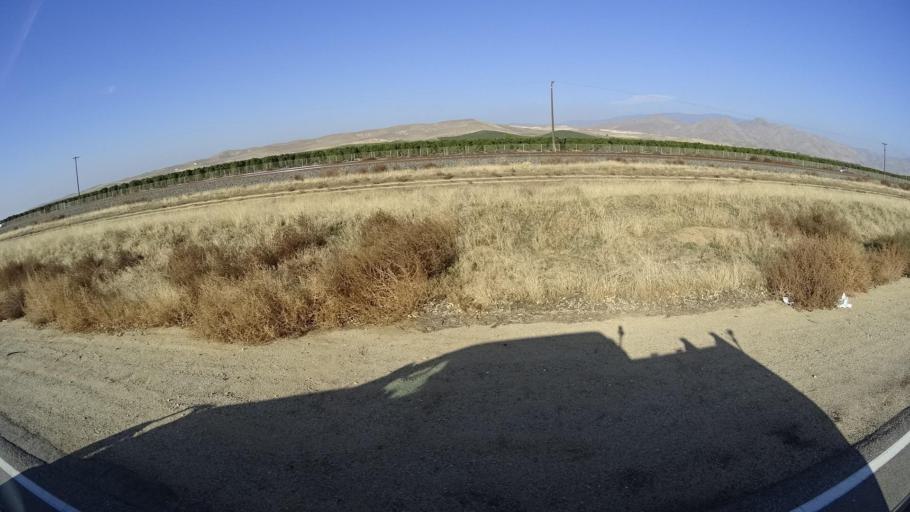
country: US
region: California
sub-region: Kern County
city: Arvin
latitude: 35.3270
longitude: -118.7842
